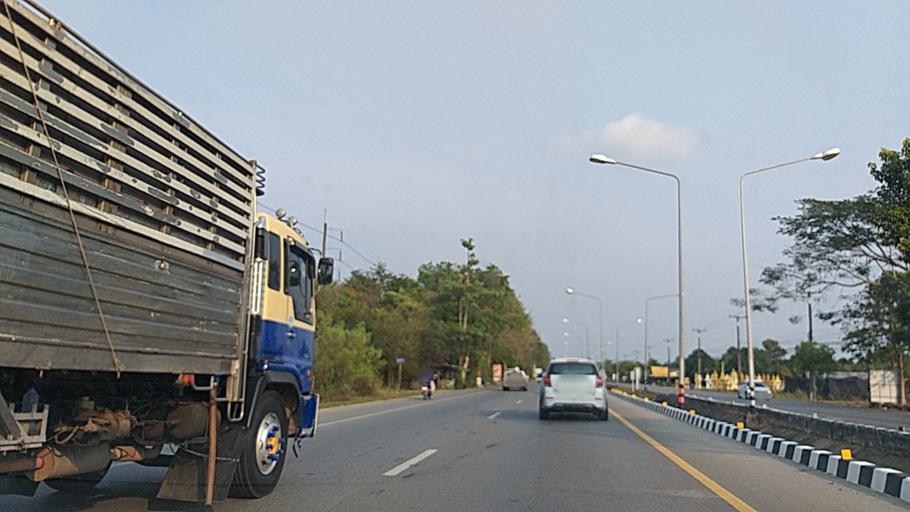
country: TH
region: Chanthaburi
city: Khlung
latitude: 12.4553
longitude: 102.2380
